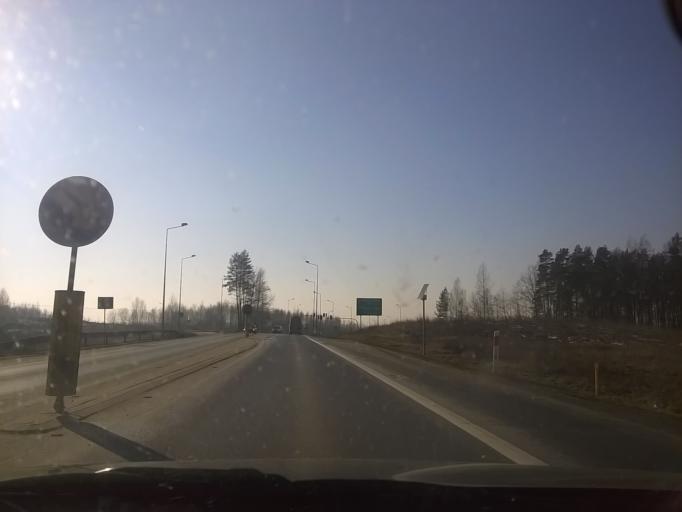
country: PL
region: Warmian-Masurian Voivodeship
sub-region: Powiat olsztynski
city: Olsztyn
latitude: 53.7796
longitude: 20.5654
